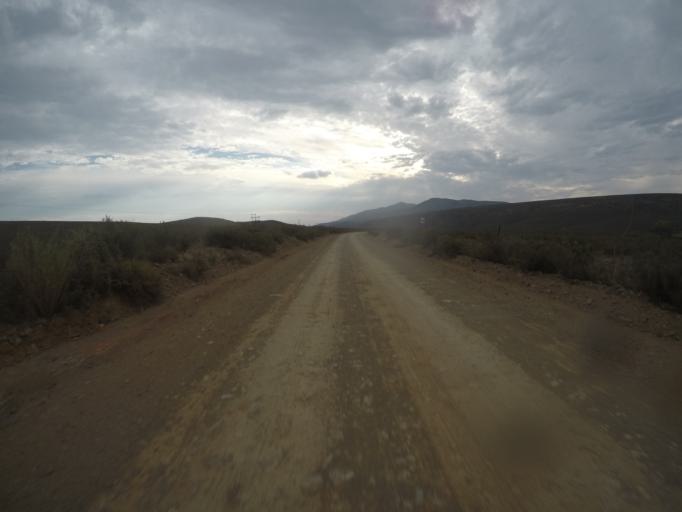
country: ZA
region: Eastern Cape
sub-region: Cacadu District Municipality
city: Willowmore
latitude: -33.4911
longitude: 23.5670
